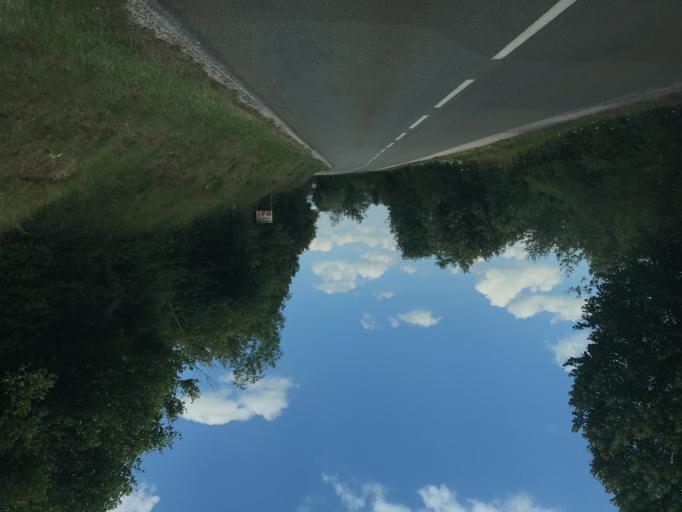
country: FR
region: Franche-Comte
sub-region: Departement du Jura
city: Clairvaux-les-Lacs
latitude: 46.5648
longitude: 5.7588
